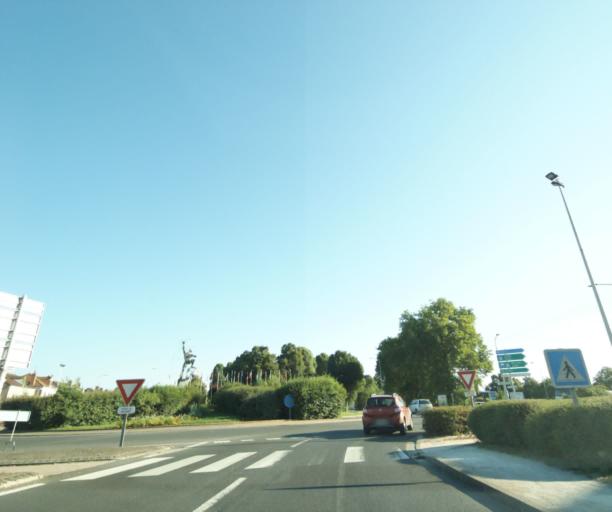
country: FR
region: Ile-de-France
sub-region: Departement de Seine-et-Marne
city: Montereau-Fault-Yonne
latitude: 48.3778
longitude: 2.9565
